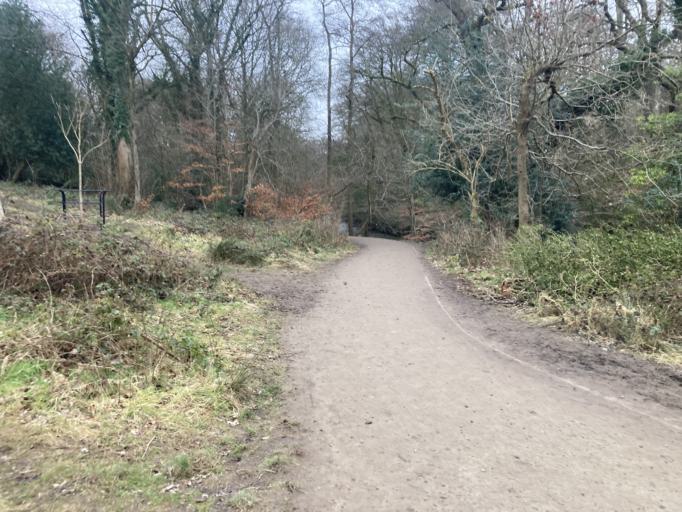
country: GB
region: England
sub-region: Manchester
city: Ringway
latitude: 53.3450
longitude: -2.2557
